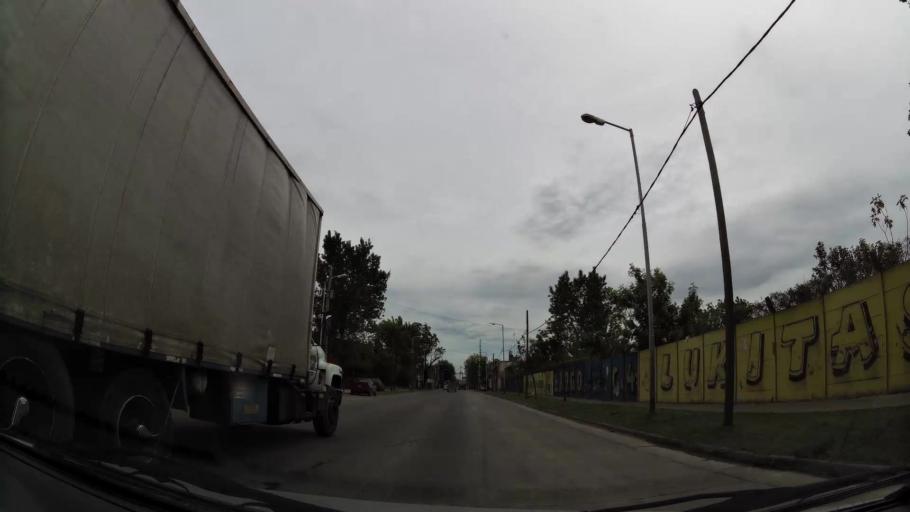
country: AR
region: Buenos Aires
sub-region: Partido de Avellaneda
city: Avellaneda
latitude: -34.6568
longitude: -58.3435
